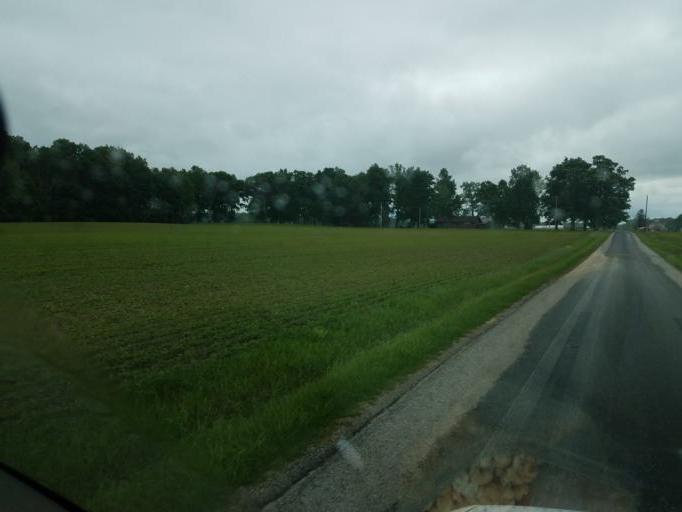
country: US
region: Ohio
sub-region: Marion County
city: Marion
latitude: 40.5547
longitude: -83.0386
